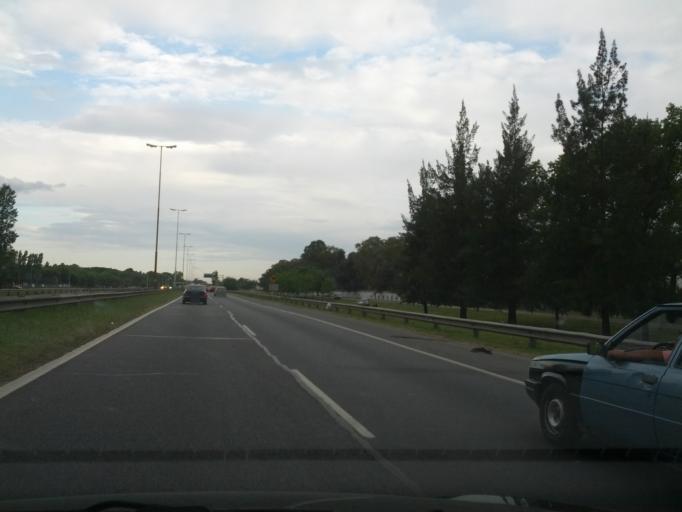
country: AR
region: Buenos Aires
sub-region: Partido de General Rodriguez
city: General Rodriguez
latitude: -34.5912
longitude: -58.9568
